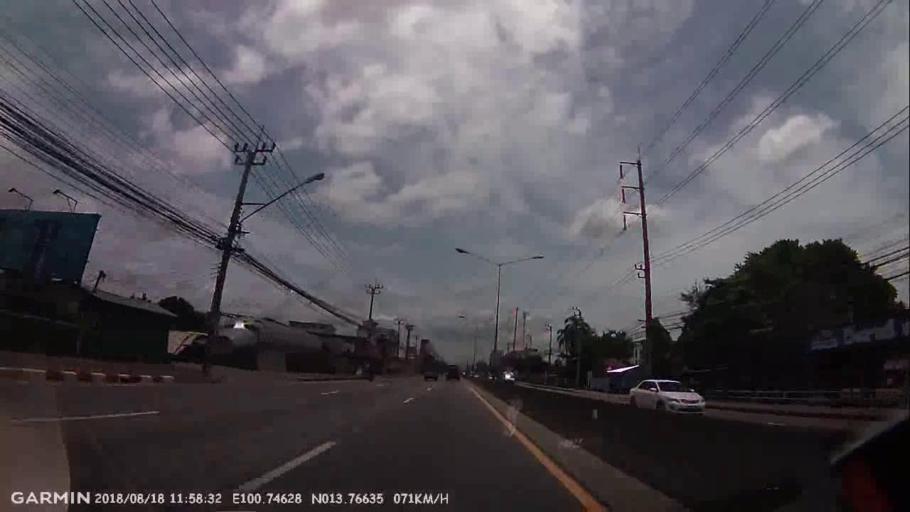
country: TH
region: Bangkok
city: Min Buri
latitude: 13.7664
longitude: 100.7463
